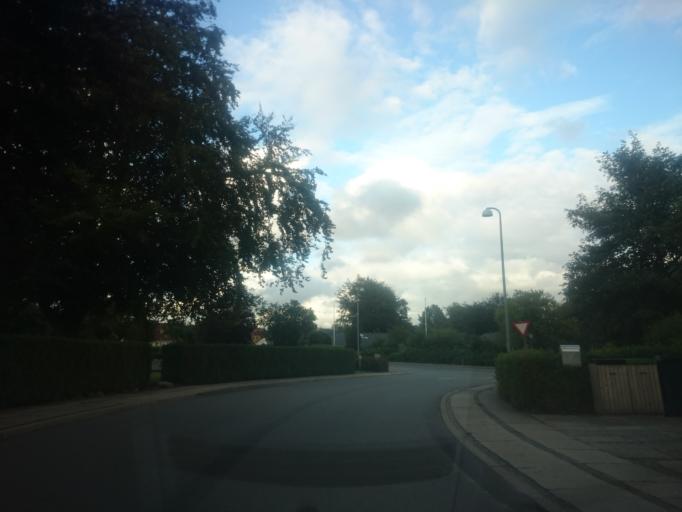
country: DK
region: South Denmark
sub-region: Billund Kommune
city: Billund
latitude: 55.6295
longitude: 9.0760
